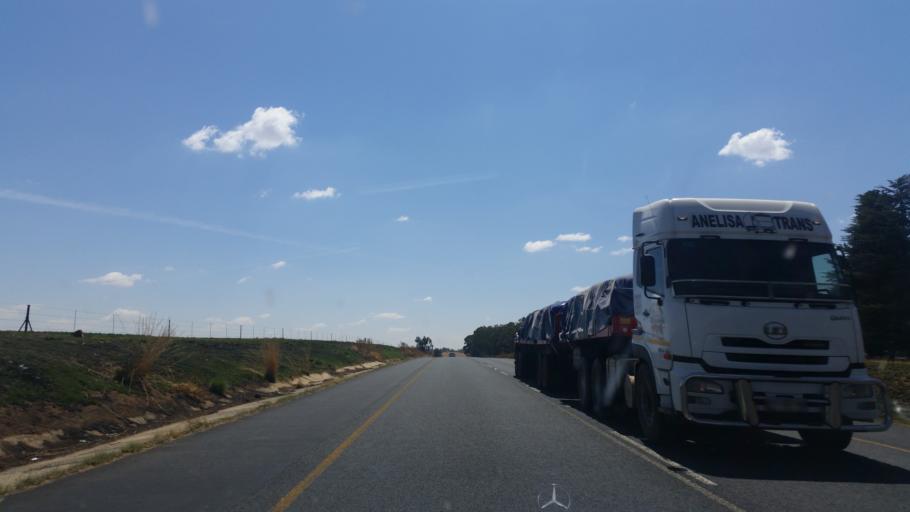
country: ZA
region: Orange Free State
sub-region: Thabo Mofutsanyana District Municipality
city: Reitz
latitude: -28.0960
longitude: 28.6562
